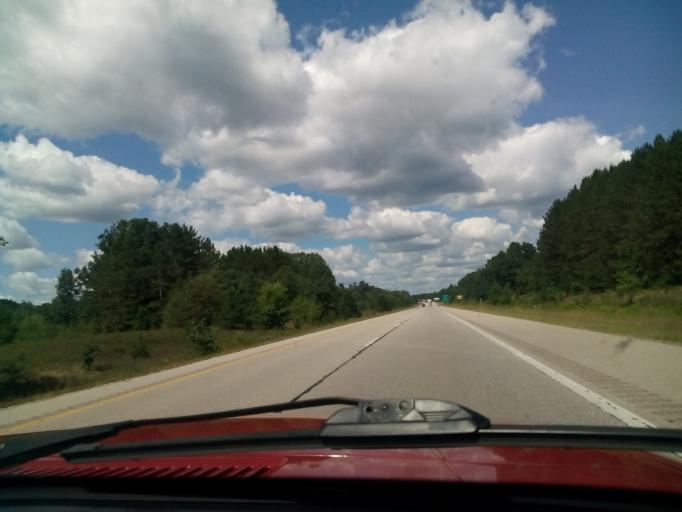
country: US
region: Michigan
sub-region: Ogemaw County
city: Skidway Lake
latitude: 44.1109
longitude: -84.1178
